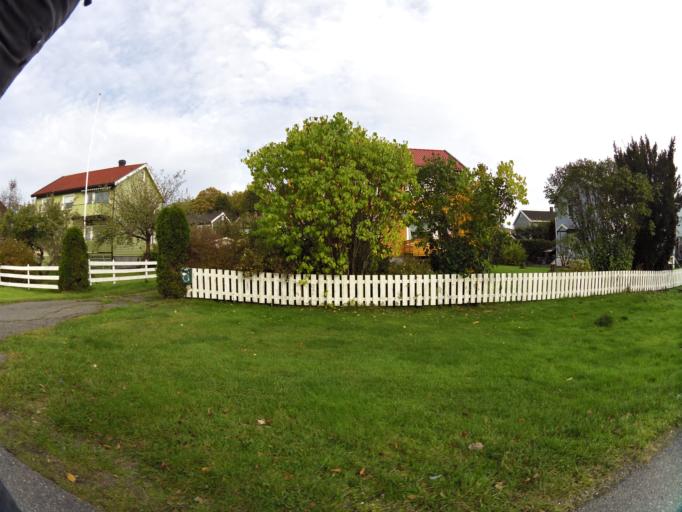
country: NO
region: Ostfold
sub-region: Fredrikstad
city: Fredrikstad
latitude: 59.2200
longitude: 10.9105
